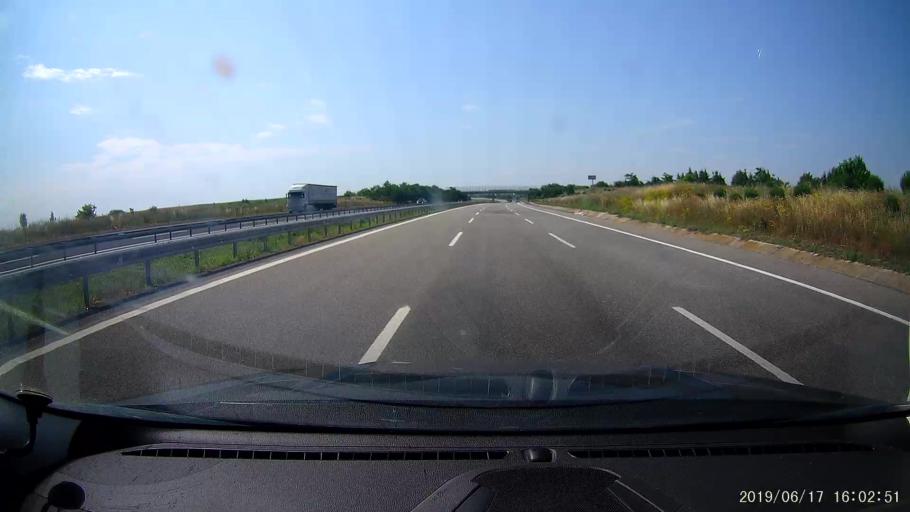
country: TR
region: Tekirdag
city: Velimese
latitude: 41.2659
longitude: 27.8132
